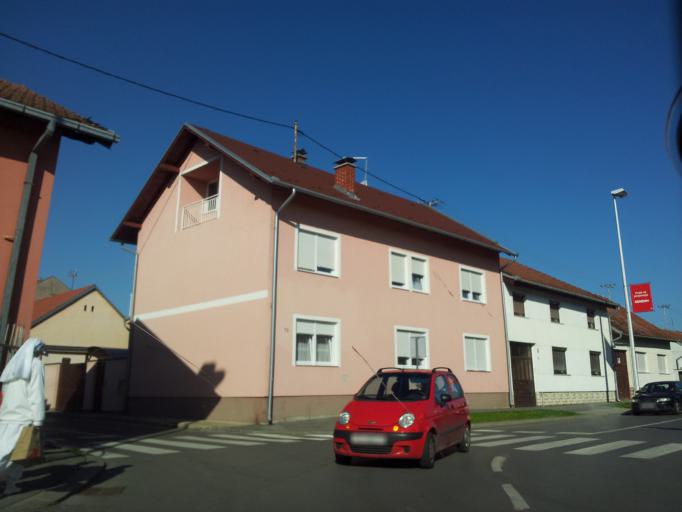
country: HR
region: Osjecko-Baranjska
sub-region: Grad Osijek
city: Osijek
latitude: 45.5488
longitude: 18.7136
